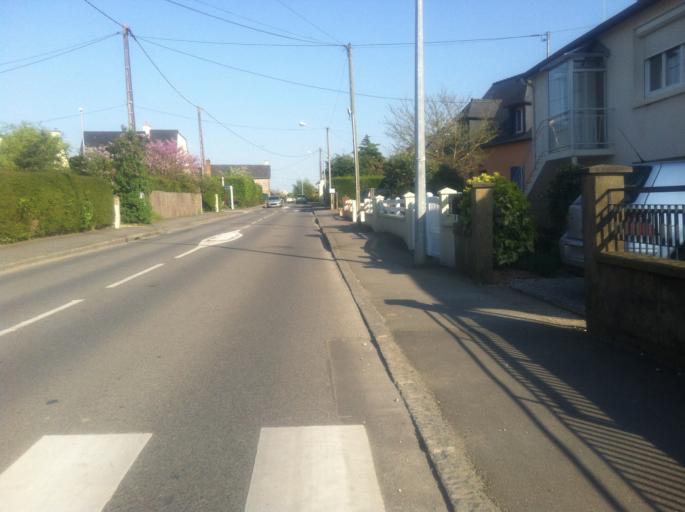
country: FR
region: Brittany
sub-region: Departement d'Ille-et-Vilaine
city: Bruz
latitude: 48.0216
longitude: -1.7322
